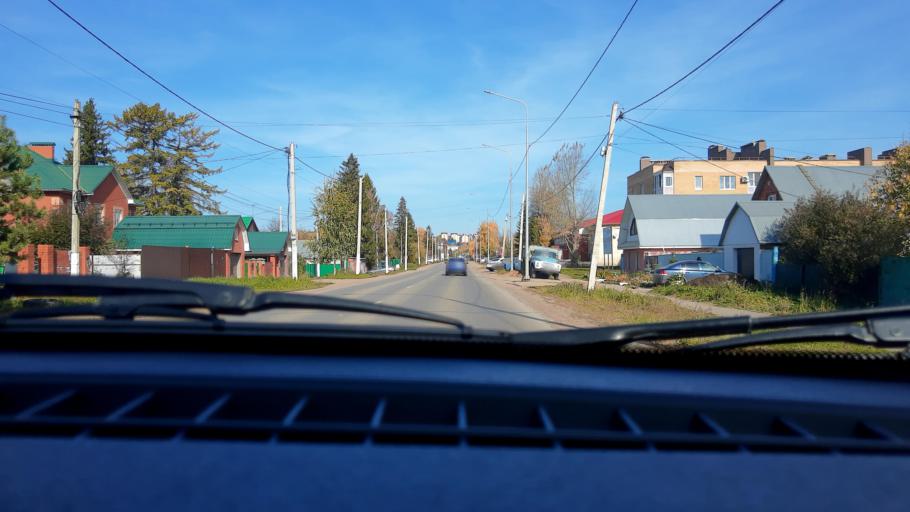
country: RU
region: Bashkortostan
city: Mikhaylovka
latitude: 54.7993
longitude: 55.8914
